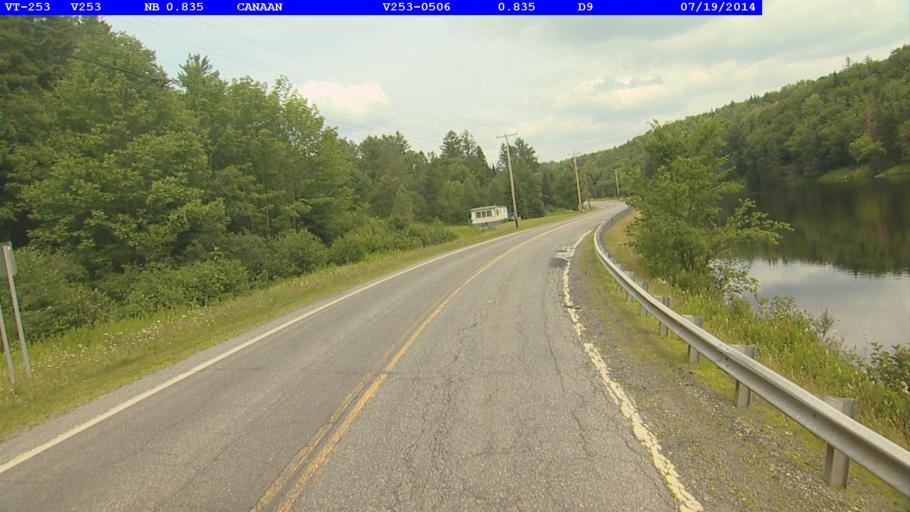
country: US
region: New Hampshire
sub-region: Coos County
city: Colebrook
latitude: 45.0025
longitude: -71.5243
